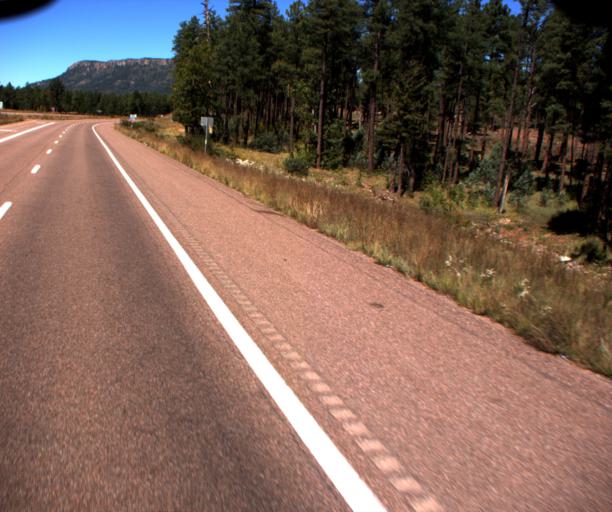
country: US
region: Arizona
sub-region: Gila County
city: Star Valley
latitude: 34.3058
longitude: -110.9943
